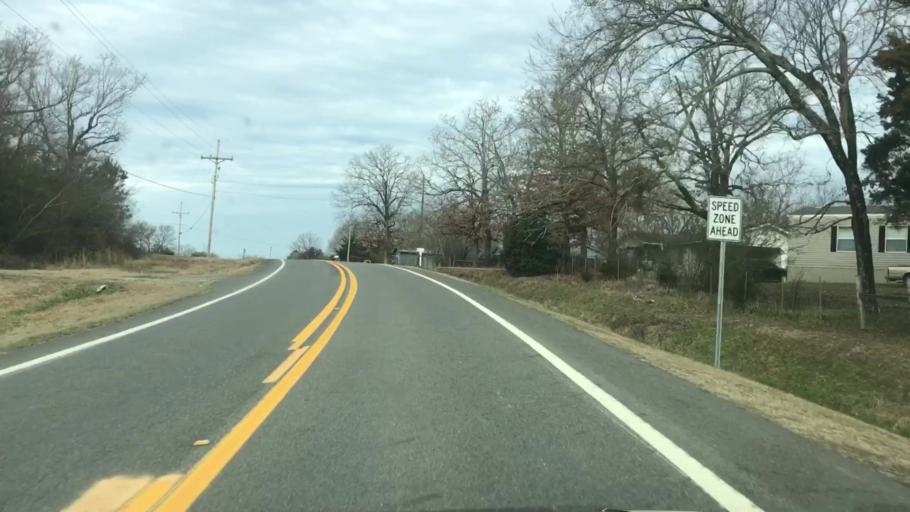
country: US
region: Arkansas
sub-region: Montgomery County
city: Mount Ida
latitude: 34.6239
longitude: -93.7271
